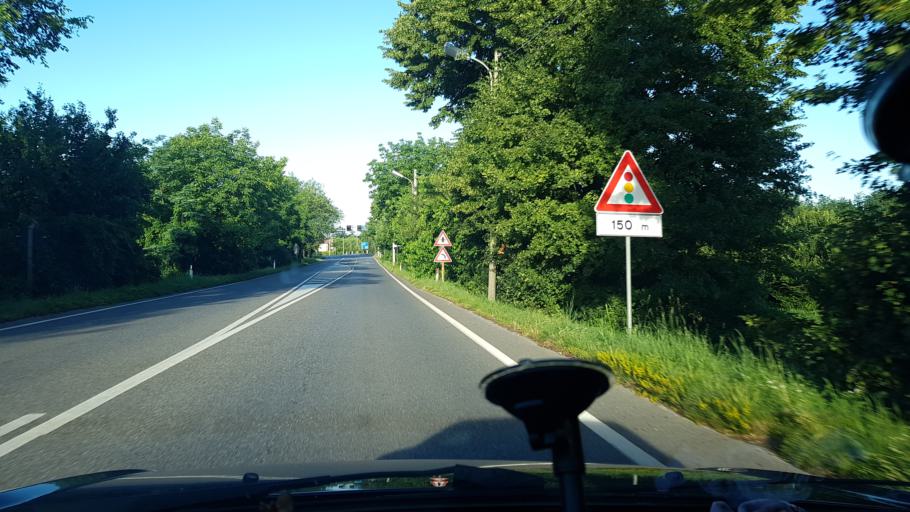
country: IT
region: Friuli Venezia Giulia
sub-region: Provincia di Gorizia
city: Savogna d'Isonzo
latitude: 45.9273
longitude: 13.5745
